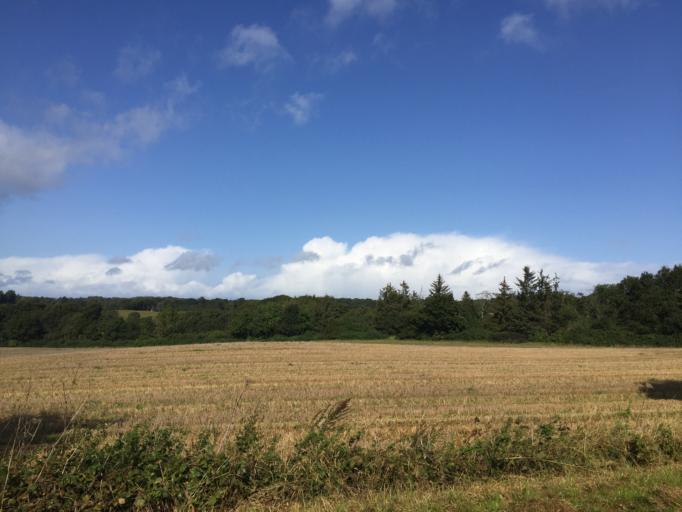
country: DK
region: South Denmark
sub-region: Assens Kommune
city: Arup
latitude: 55.3640
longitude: 9.9748
